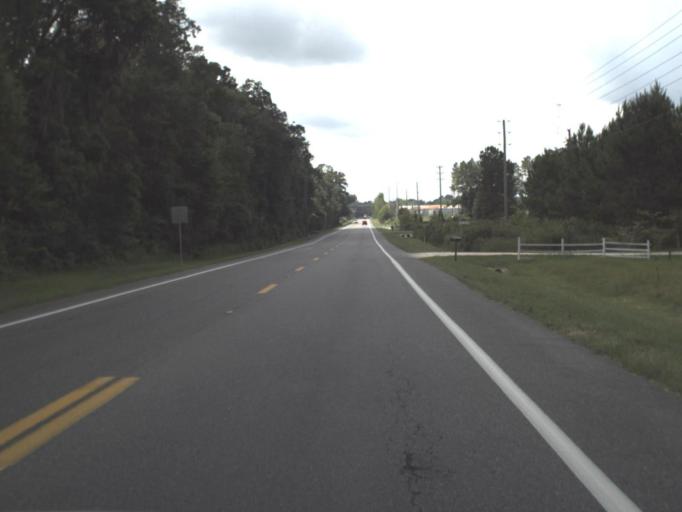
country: US
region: Florida
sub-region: Union County
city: Lake Butler
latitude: 29.9446
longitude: -82.4247
